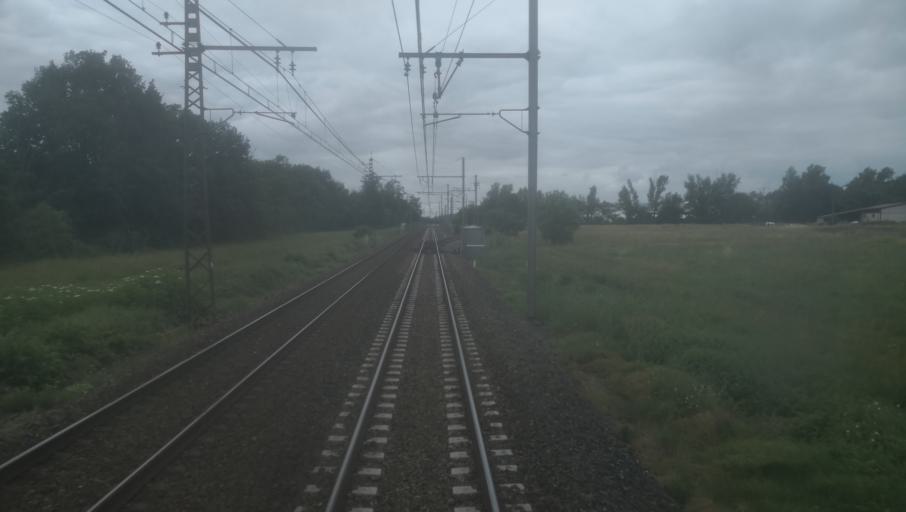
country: FR
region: Midi-Pyrenees
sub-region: Departement du Tarn-et-Garonne
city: Grisolles
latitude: 43.8413
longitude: 1.2927
